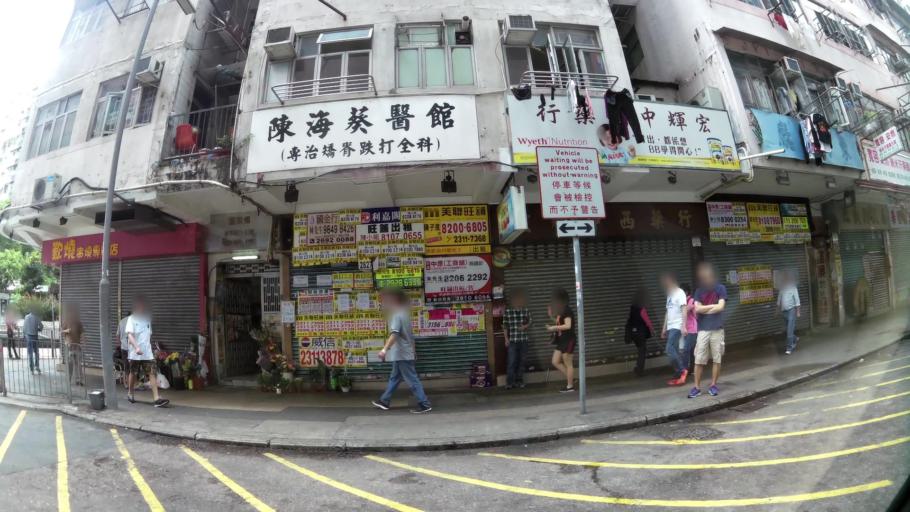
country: HK
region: Wong Tai Sin
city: Wong Tai Sin
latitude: 22.3351
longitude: 114.1956
